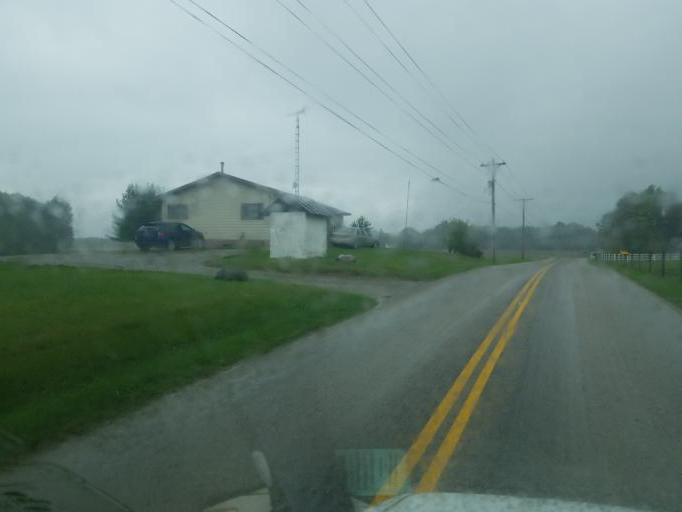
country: US
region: Ohio
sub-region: Wayne County
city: Shreve
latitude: 40.6348
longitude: -82.0160
